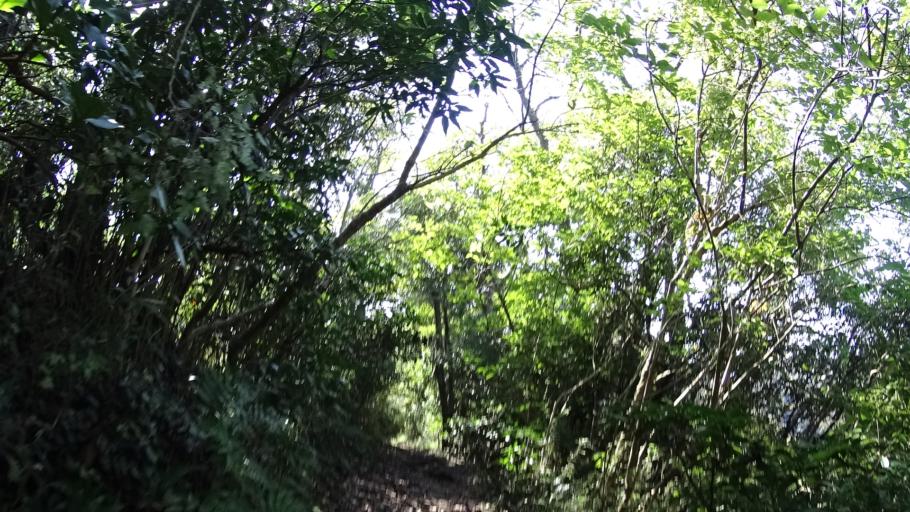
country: JP
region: Kanagawa
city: Yokosuka
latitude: 35.2776
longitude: 139.6244
